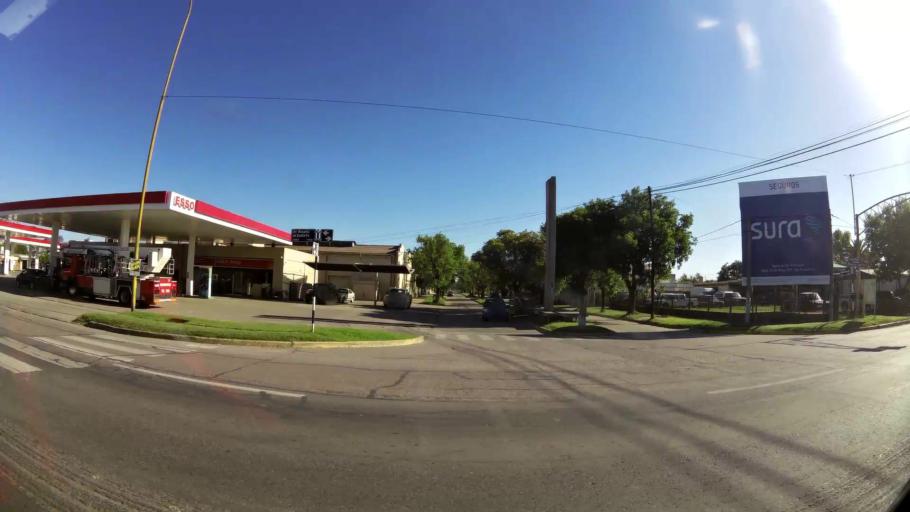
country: AR
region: Cordoba
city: San Francisco
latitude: -31.4167
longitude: -62.0823
